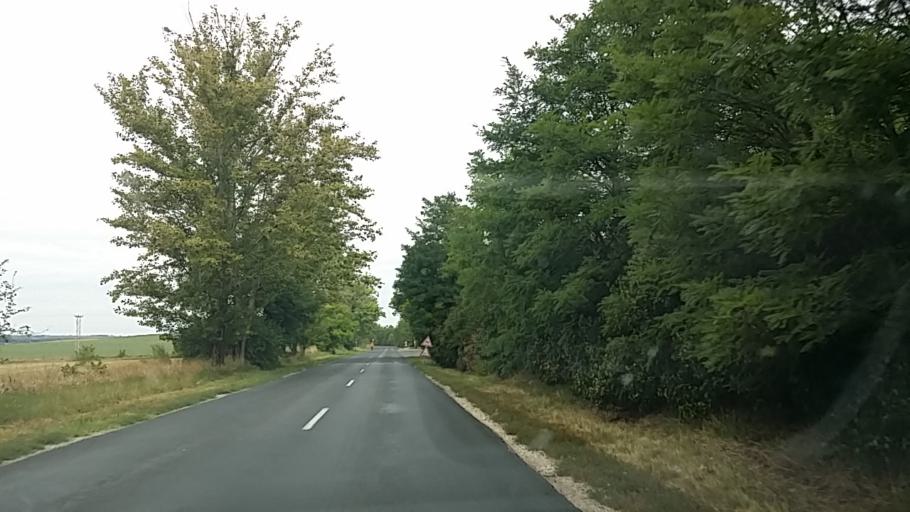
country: HU
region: Komarom-Esztergom
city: Naszaly
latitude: 47.6638
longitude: 18.2653
